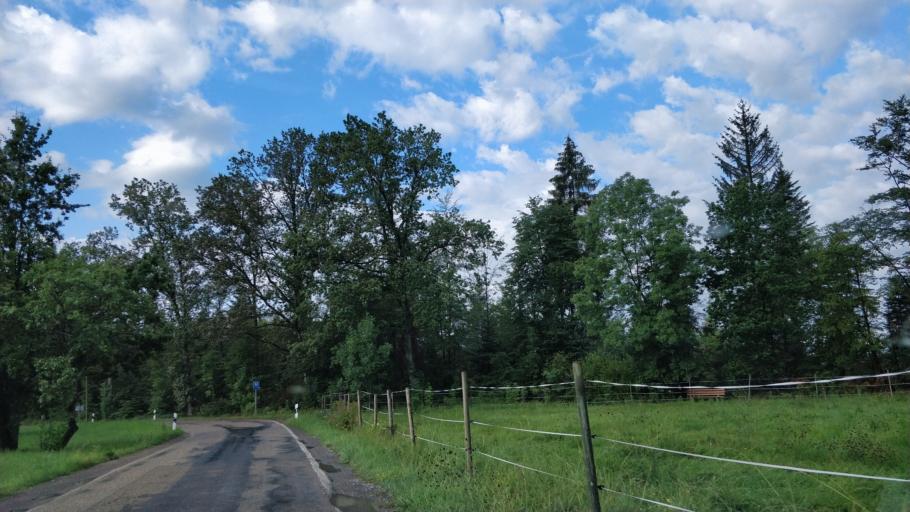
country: DE
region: Baden-Wuerttemberg
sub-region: Regierungsbezirk Stuttgart
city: Fichtenberg
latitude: 48.9747
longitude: 9.6798
